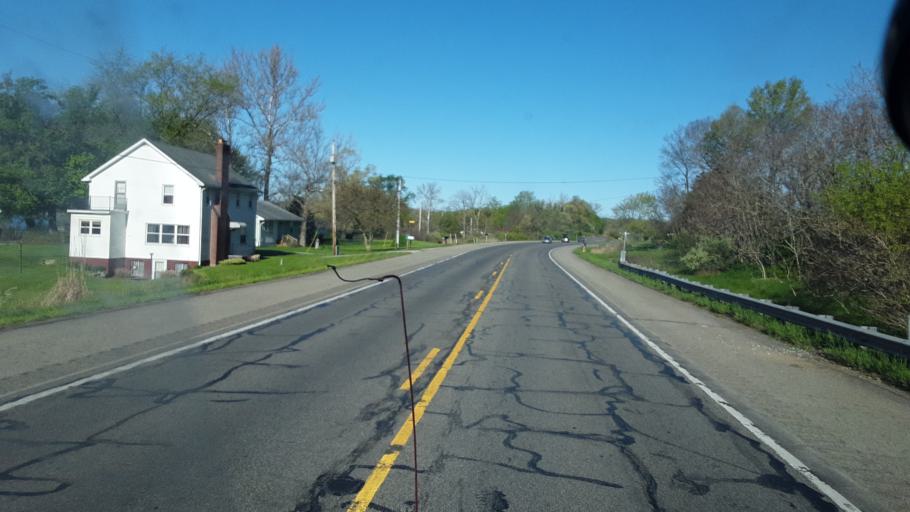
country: US
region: Indiana
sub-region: Steuben County
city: Angola
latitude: 41.6349
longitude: -85.0608
